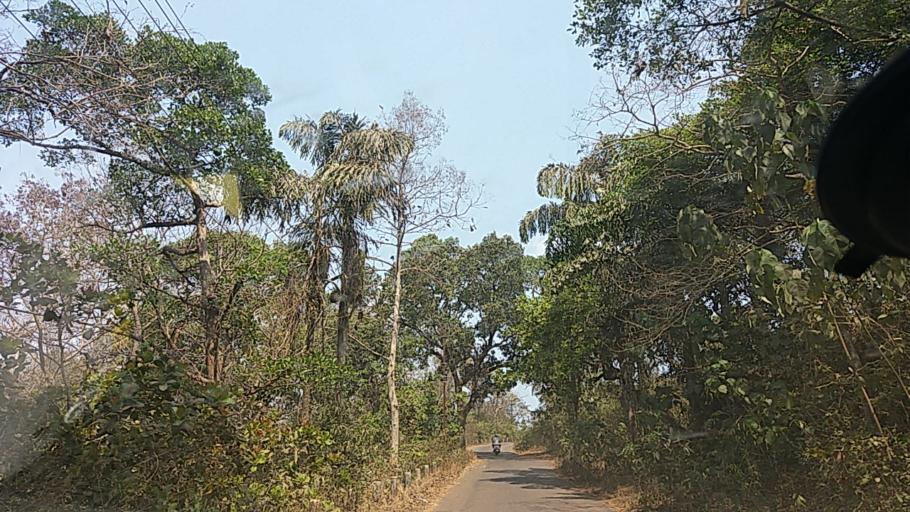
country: IN
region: Goa
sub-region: South Goa
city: Sancoale
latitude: 15.3755
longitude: 73.9132
